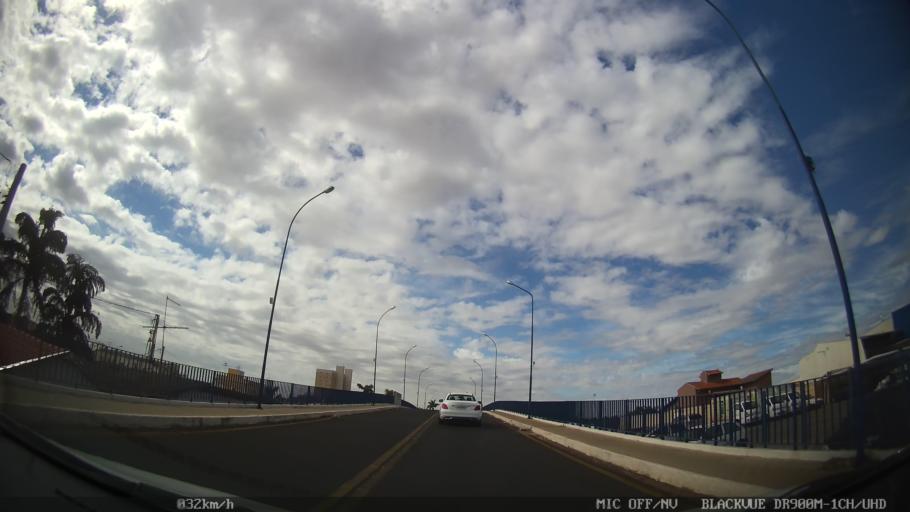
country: BR
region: Sao Paulo
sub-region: Bady Bassitt
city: Bady Bassitt
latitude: -20.8135
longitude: -49.5086
